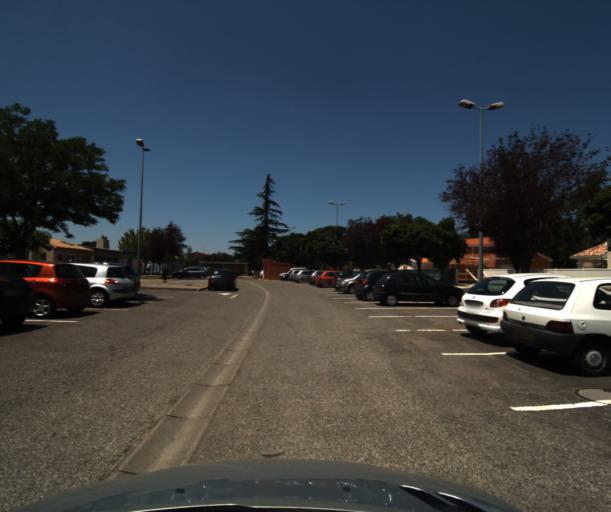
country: FR
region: Midi-Pyrenees
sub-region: Departement de la Haute-Garonne
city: Roquettes
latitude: 43.4943
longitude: 1.3762
